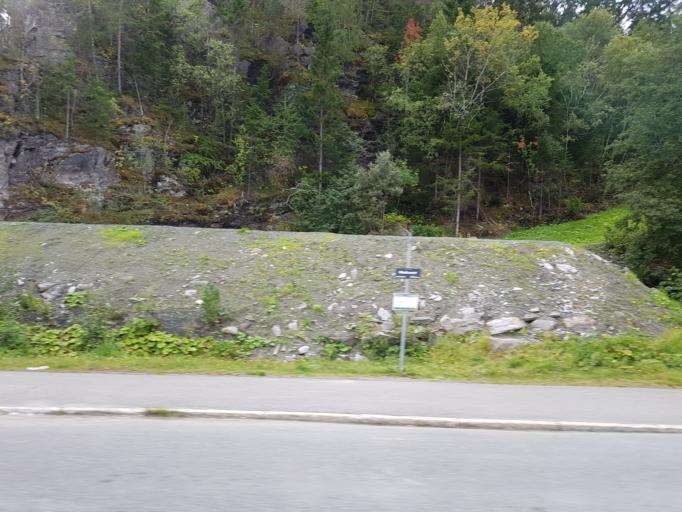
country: NO
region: Sor-Trondelag
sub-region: Trondheim
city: Trondheim
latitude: 63.4491
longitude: 10.3189
